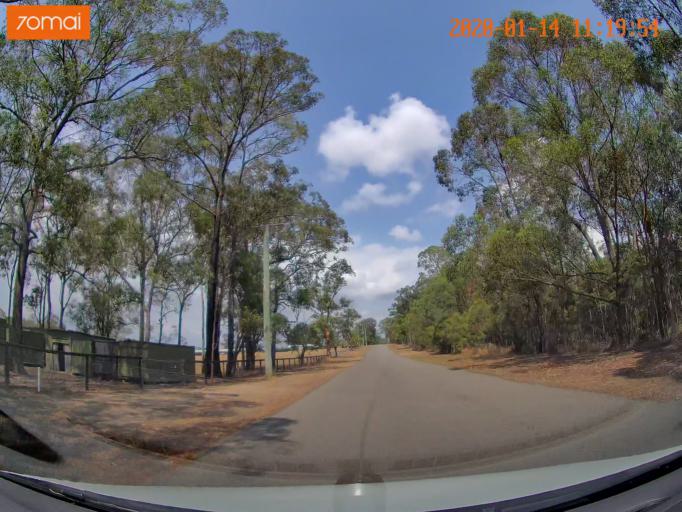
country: AU
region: New South Wales
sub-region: Lake Macquarie Shire
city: Cooranbong
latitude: -33.1001
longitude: 151.4592
